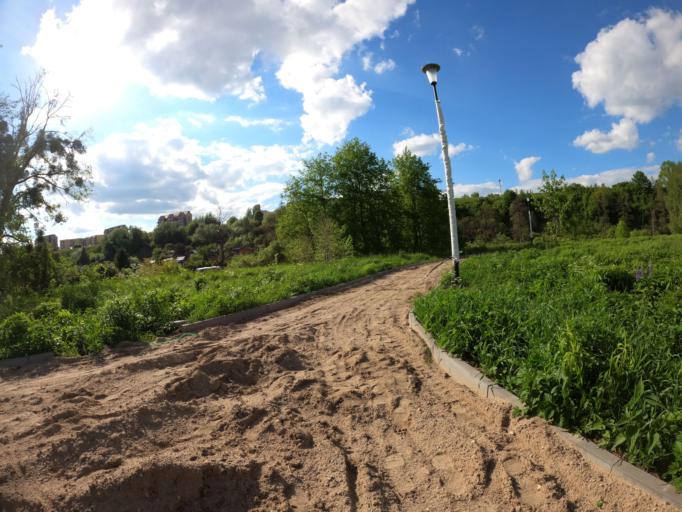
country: PL
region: Warmian-Masurian Voivodeship
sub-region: Powiat lidzbarski
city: Lidzbark Warminski
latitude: 54.1341
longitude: 20.5970
